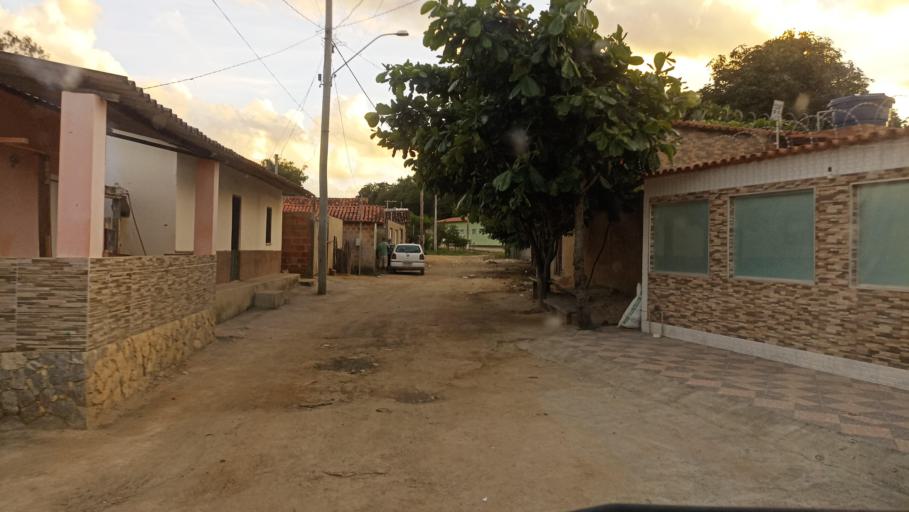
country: BR
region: Minas Gerais
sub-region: Almenara
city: Almenara
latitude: -16.5198
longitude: -40.4414
